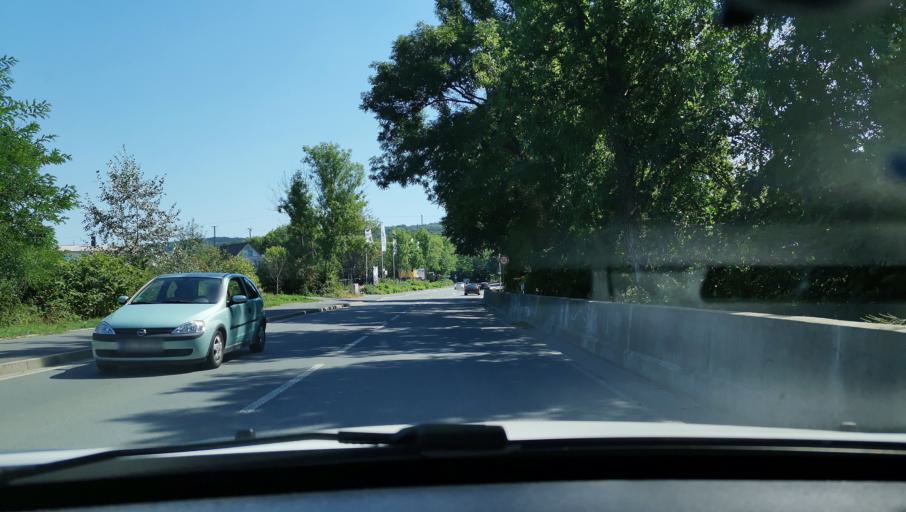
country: DE
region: North Rhine-Westphalia
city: Wetter (Ruhr)
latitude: 51.3809
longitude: 7.4116
